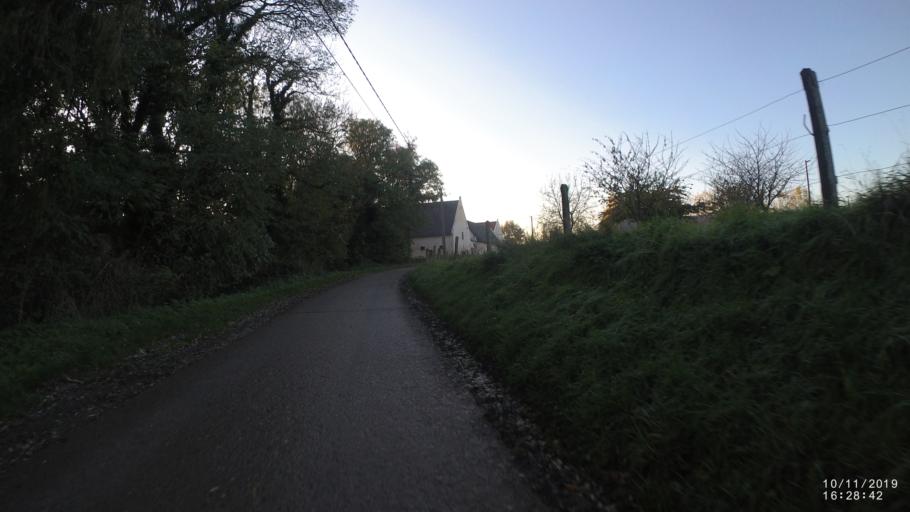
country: BE
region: Flanders
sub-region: Provincie Vlaams-Brabant
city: Lubbeek
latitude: 50.8718
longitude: 4.8107
